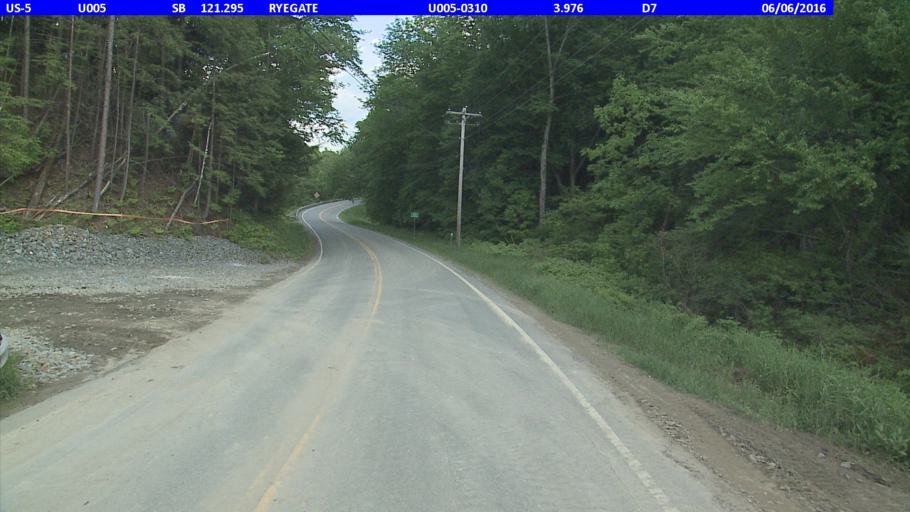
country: US
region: New Hampshire
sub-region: Grafton County
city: Woodsville
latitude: 44.2090
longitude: -72.0615
